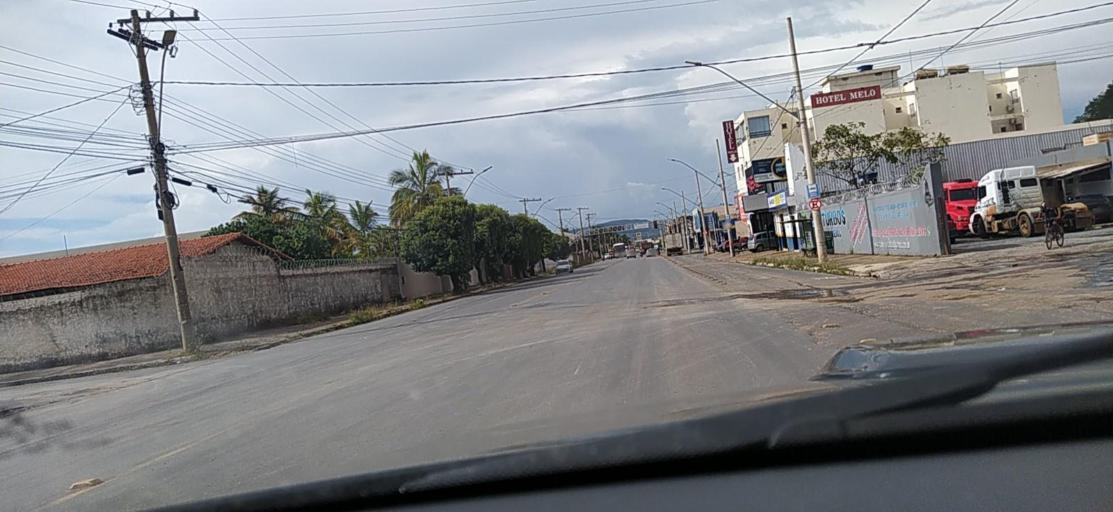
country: BR
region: Minas Gerais
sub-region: Montes Claros
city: Montes Claros
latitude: -16.7372
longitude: -43.8462
